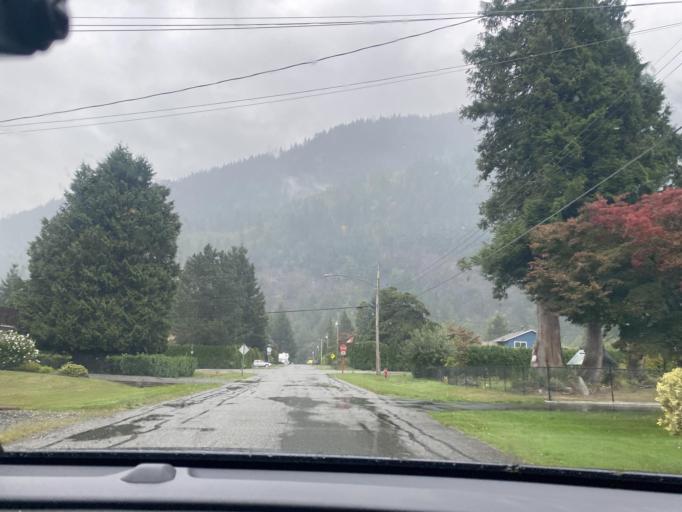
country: CA
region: British Columbia
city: Agassiz
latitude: 49.2997
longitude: -121.7774
